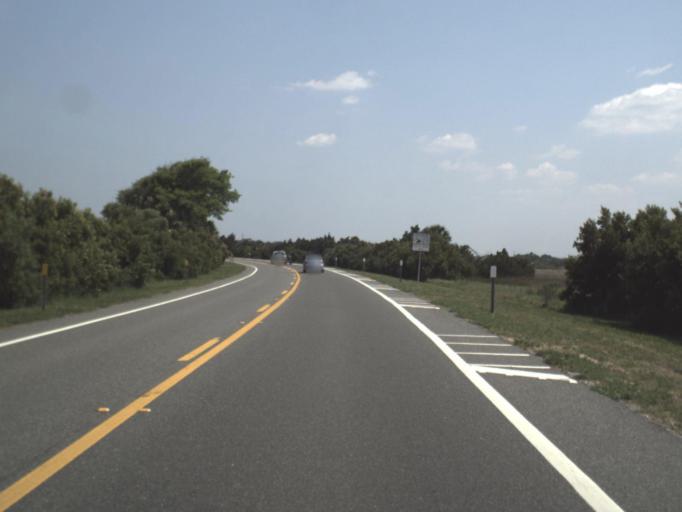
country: US
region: Florida
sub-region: Duval County
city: Atlantic Beach
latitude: 30.3750
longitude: -81.4358
